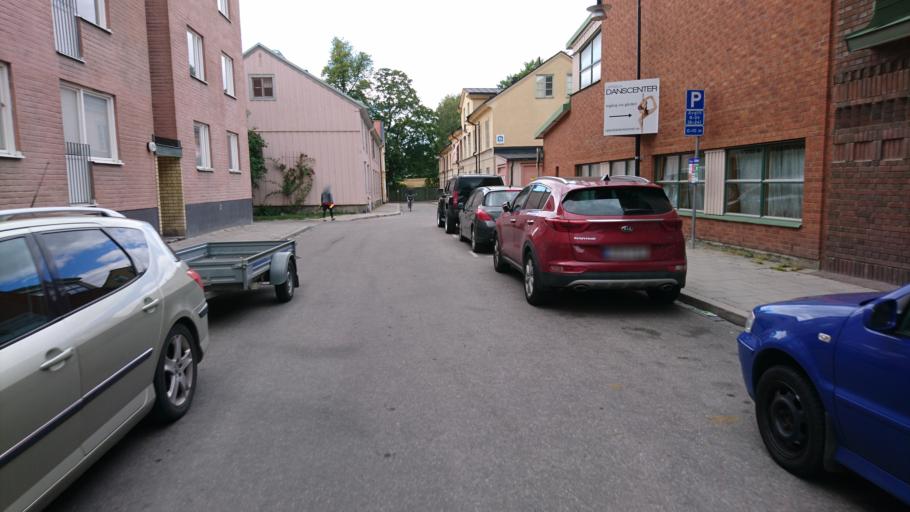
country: SE
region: Uppsala
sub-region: Uppsala Kommun
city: Uppsala
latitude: 59.8616
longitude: 17.6360
